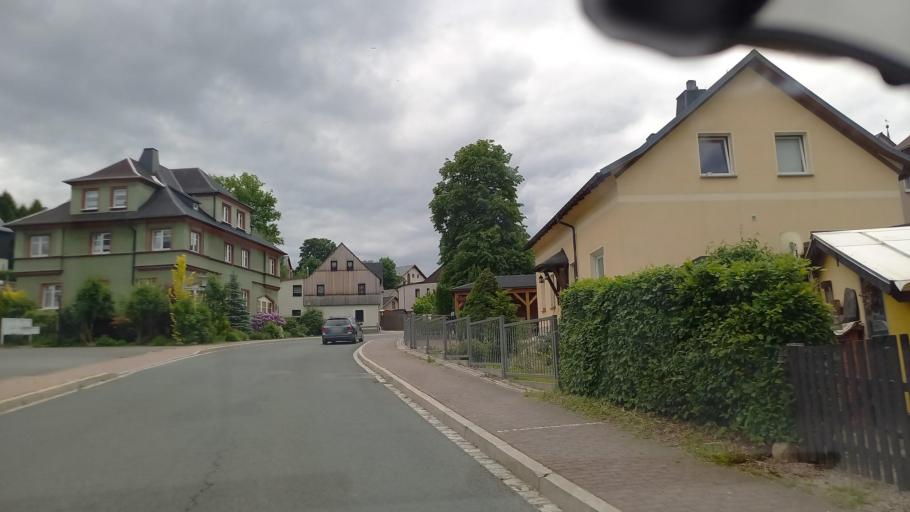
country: DE
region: Saxony
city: Stutzengrun
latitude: 50.5447
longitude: 12.5068
